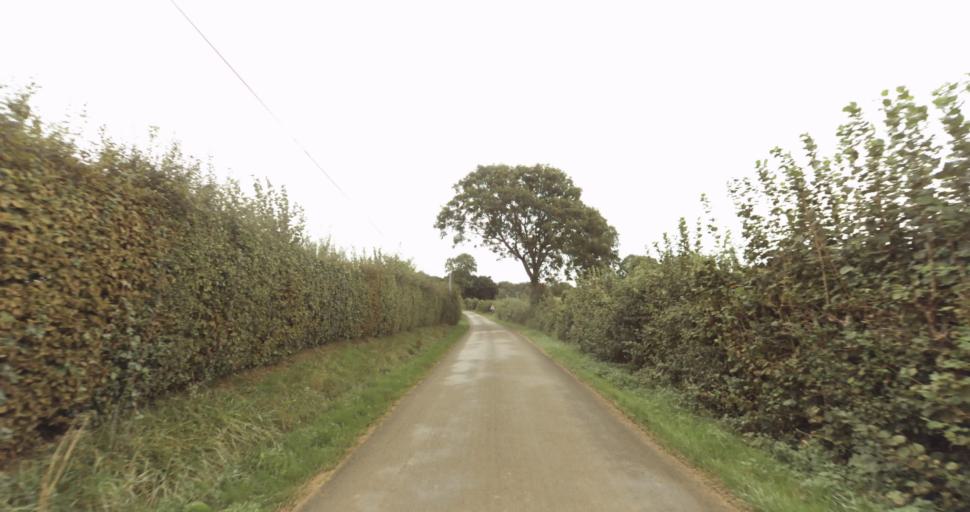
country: FR
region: Lower Normandy
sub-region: Departement de l'Orne
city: Gace
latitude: 48.7228
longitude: 0.3212
